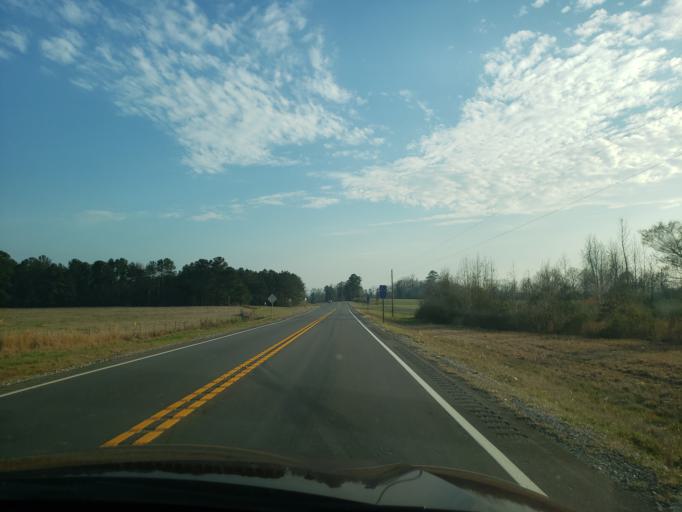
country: US
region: Alabama
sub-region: Hale County
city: Moundville
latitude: 32.8692
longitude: -87.6122
